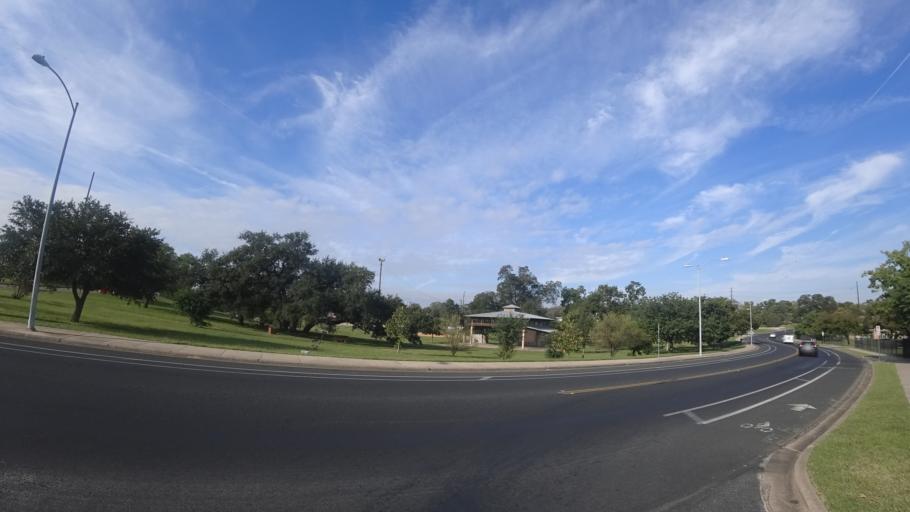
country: US
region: Texas
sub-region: Travis County
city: Austin
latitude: 30.2730
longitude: -97.7137
